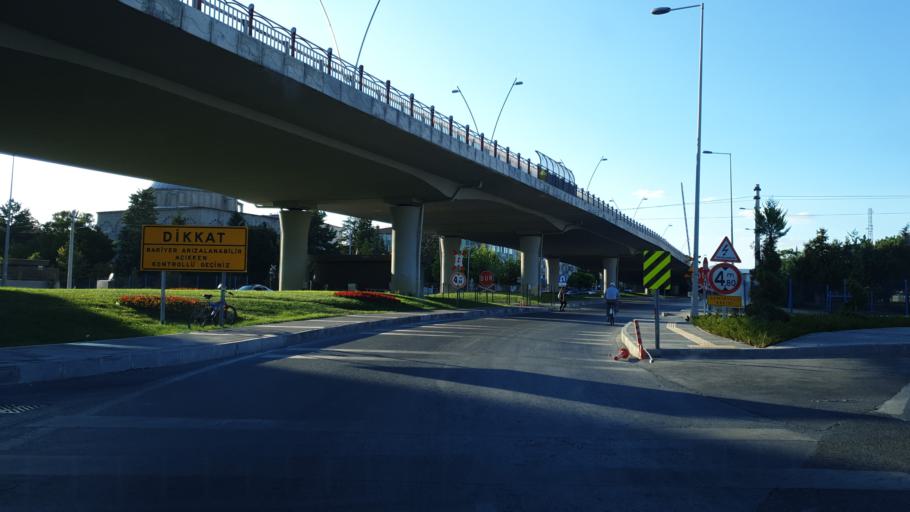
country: TR
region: Kayseri
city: Kayseri
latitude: 38.7352
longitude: 35.4936
